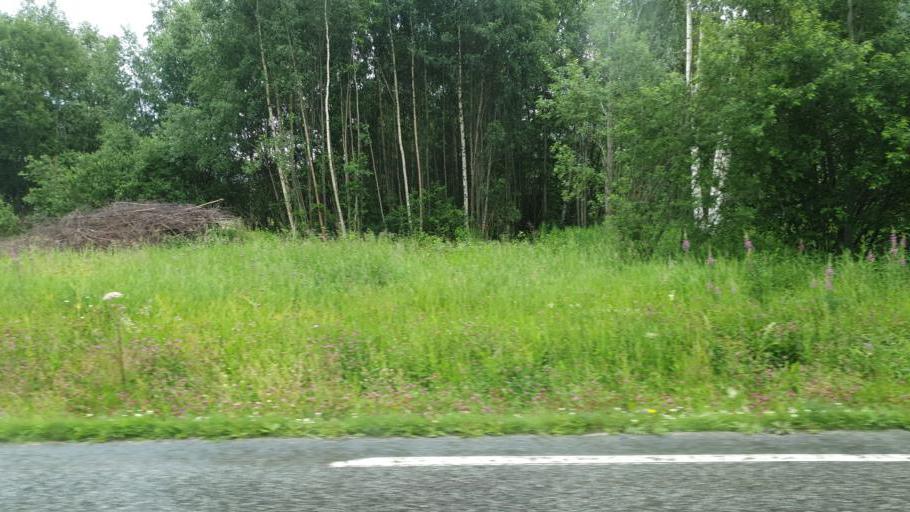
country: NO
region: Oppland
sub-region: Sel
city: Otta
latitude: 61.8456
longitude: 9.4151
